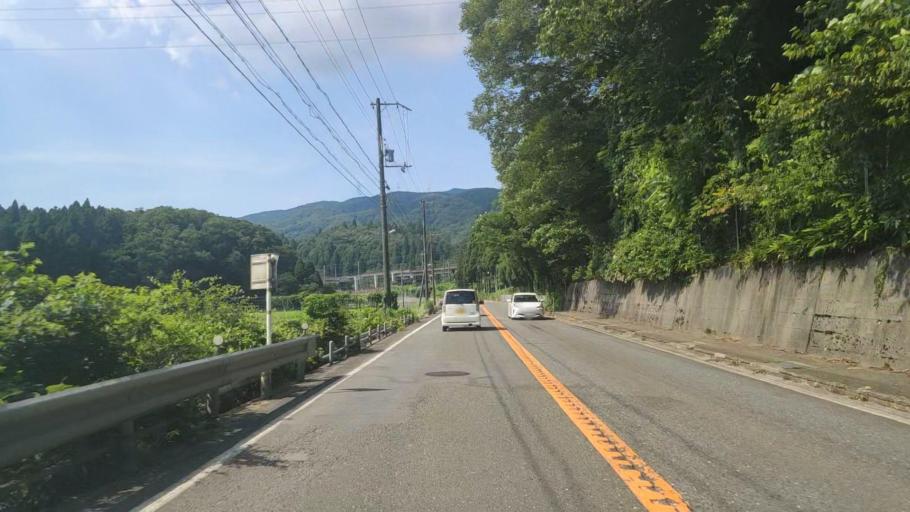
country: JP
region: Fukui
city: Tsuruga
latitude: 35.5475
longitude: 136.1477
